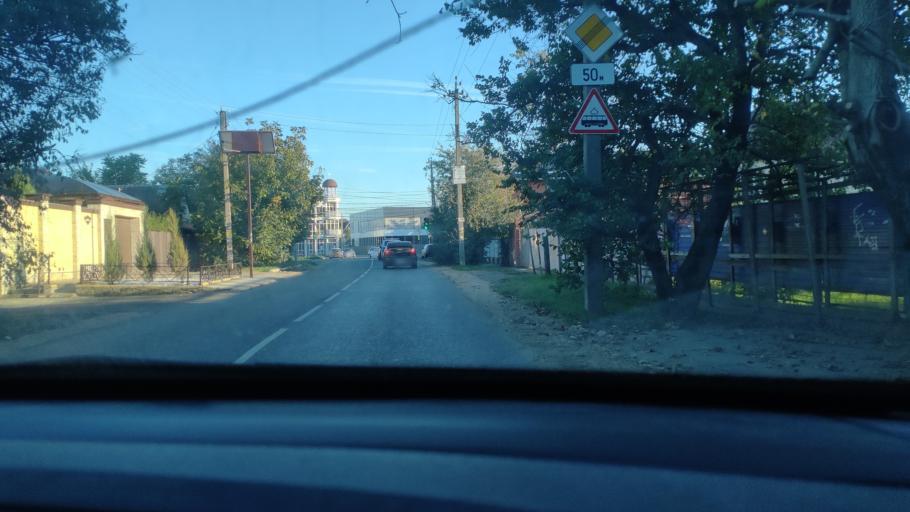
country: RU
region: Adygeya
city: Yablonovskiy
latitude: 45.0367
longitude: 38.9251
